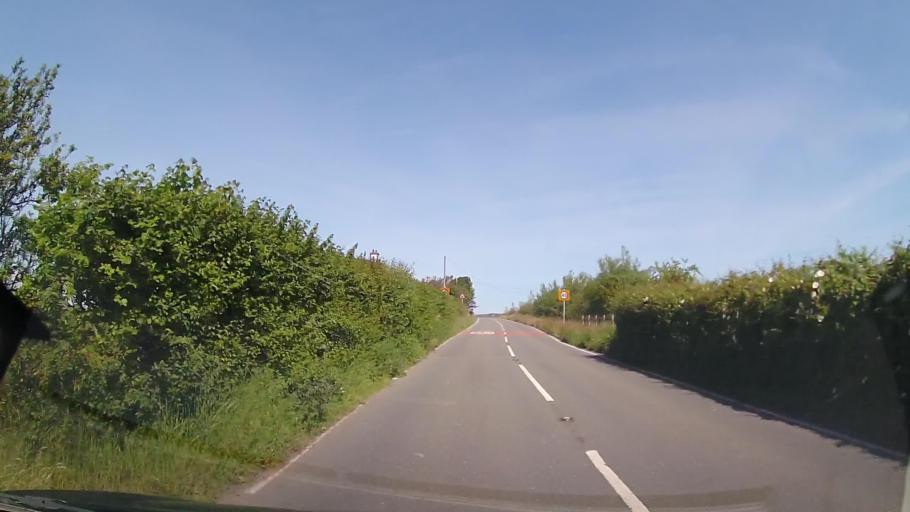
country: GB
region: Wales
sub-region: Gwynedd
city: Tywyn
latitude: 52.5778
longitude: -4.0737
